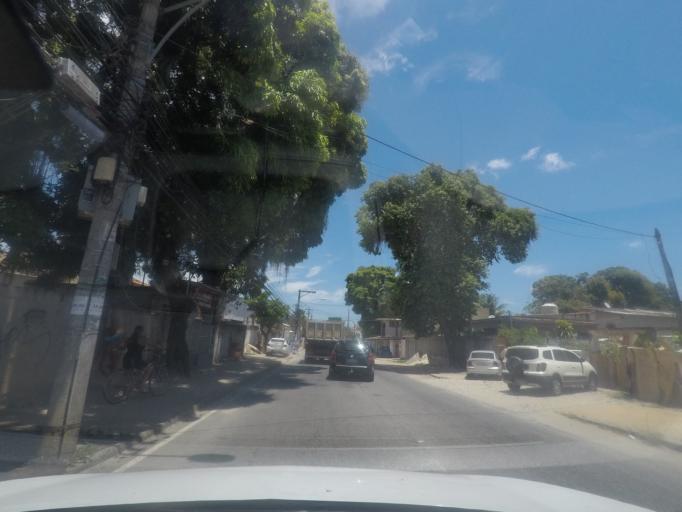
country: BR
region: Rio de Janeiro
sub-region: Itaguai
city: Itaguai
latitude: -22.9330
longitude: -43.6902
